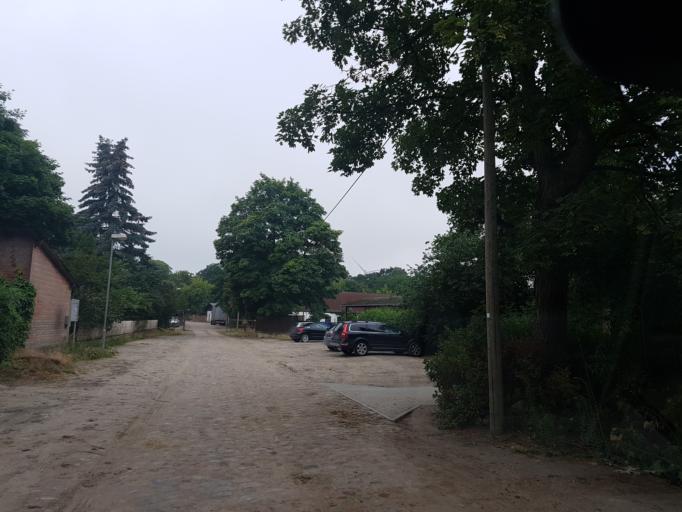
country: DE
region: Brandenburg
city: Grossbeeren
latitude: 52.3506
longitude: 13.2772
